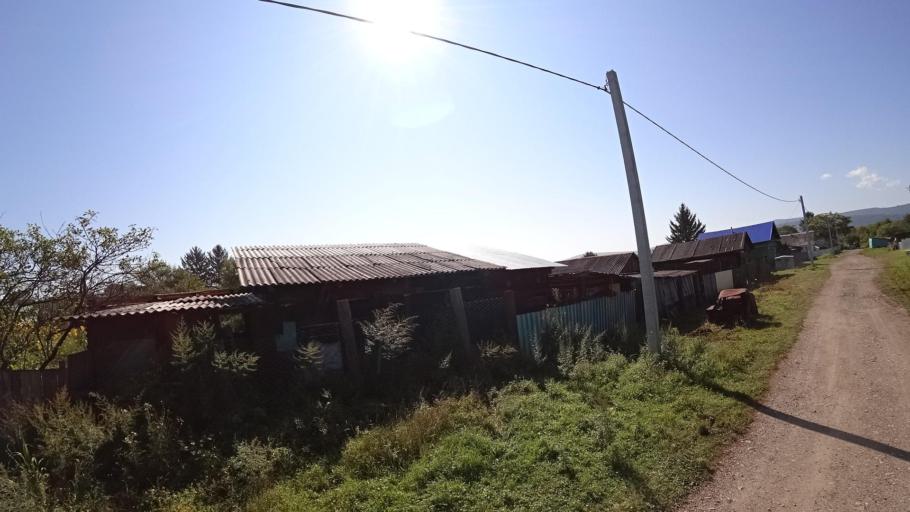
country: RU
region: Jewish Autonomous Oblast
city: Bira
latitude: 48.9983
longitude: 132.4501
